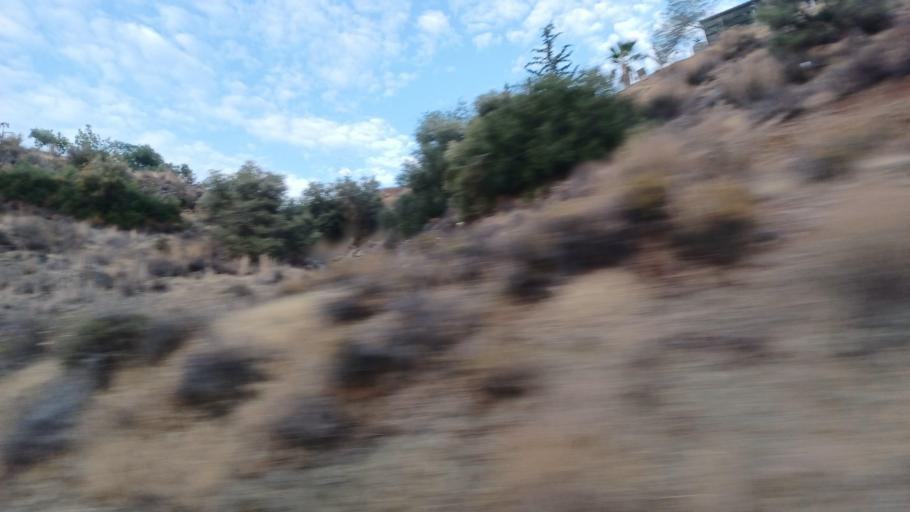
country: CY
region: Limassol
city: Pelendri
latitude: 34.8423
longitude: 32.9518
